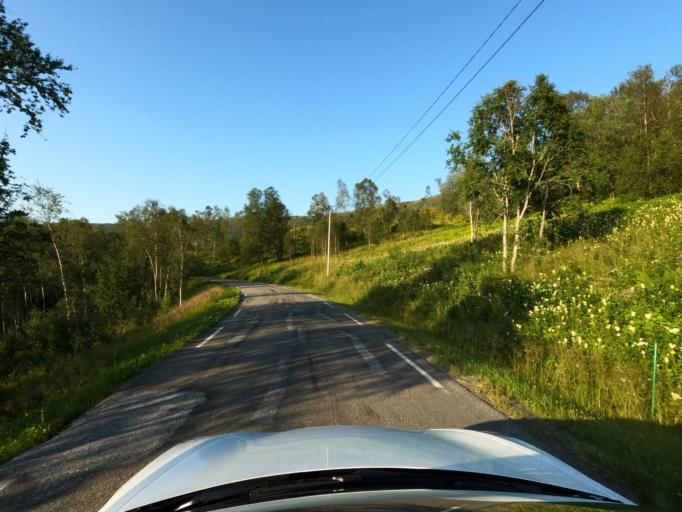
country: NO
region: Nordland
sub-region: Ballangen
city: Ballangen
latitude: 68.5216
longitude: 16.7616
